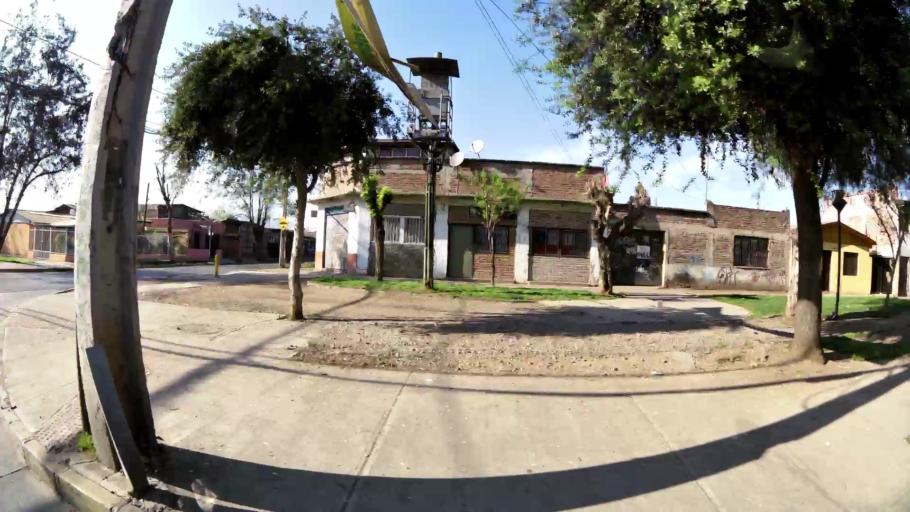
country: CL
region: Santiago Metropolitan
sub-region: Provincia de Santiago
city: Santiago
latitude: -33.3840
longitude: -70.6704
